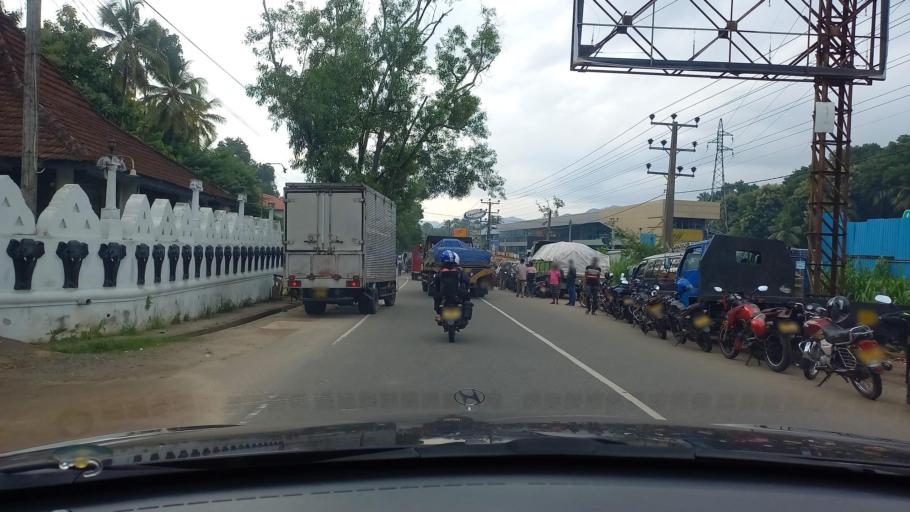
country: LK
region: Central
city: Kadugannawa
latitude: 7.2497
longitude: 80.4540
